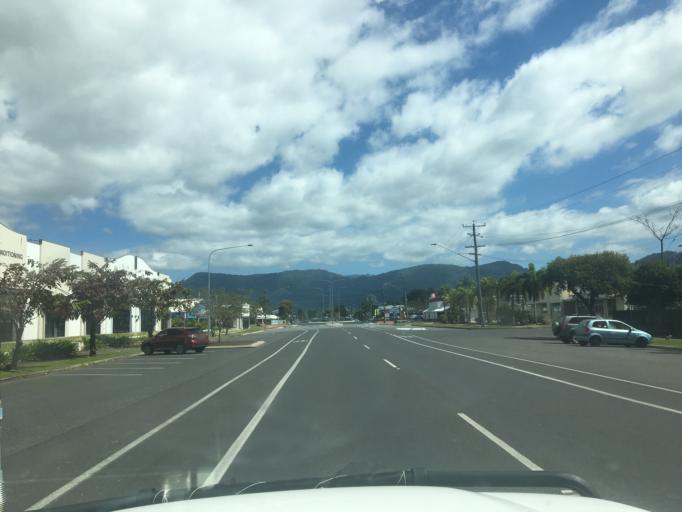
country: AU
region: Queensland
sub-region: Cairns
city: Cairns
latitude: -16.9322
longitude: 145.7625
